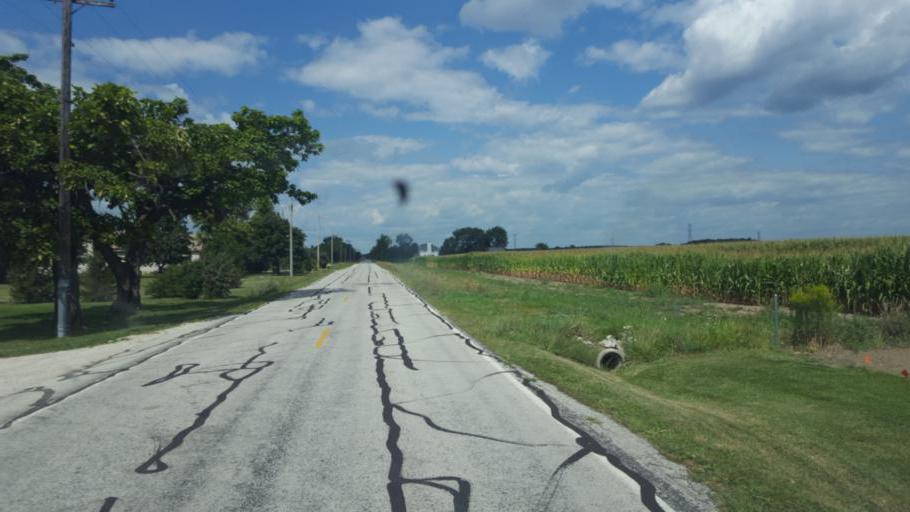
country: US
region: Ohio
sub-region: Lucas County
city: Curtice
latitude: 41.5946
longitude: -83.2804
